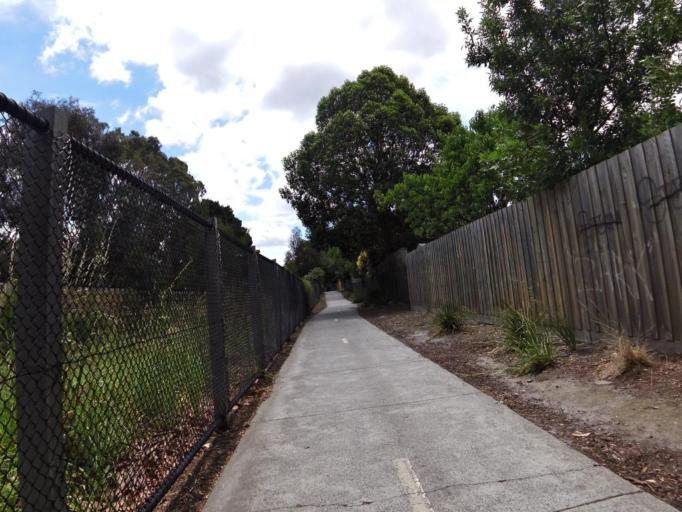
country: AU
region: Victoria
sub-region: Monash
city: Ashwood
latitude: -37.8617
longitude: 145.1013
